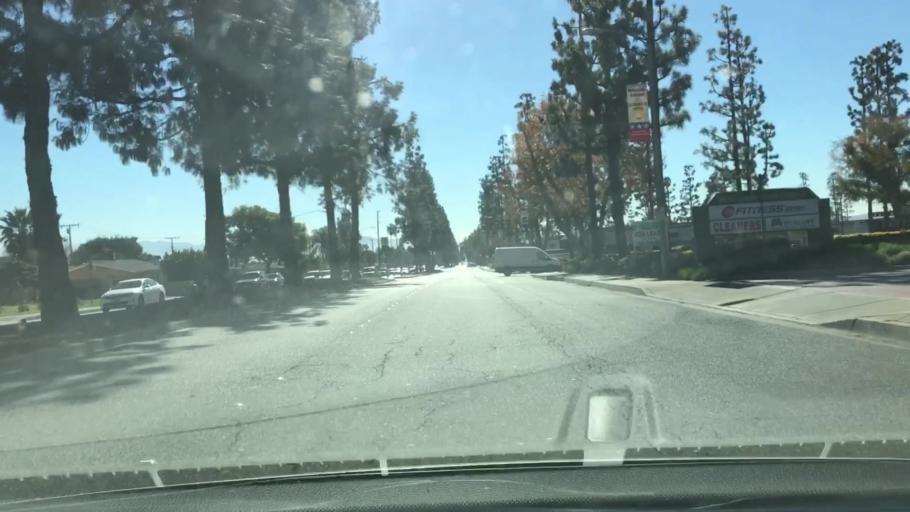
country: US
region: California
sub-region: San Bernardino County
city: Montclair
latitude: 34.0766
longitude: -117.6896
